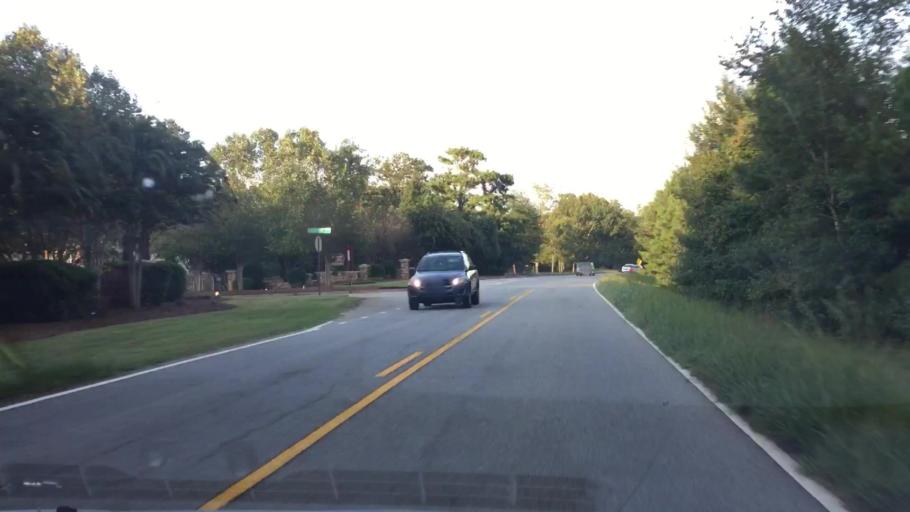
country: US
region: Georgia
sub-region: Henry County
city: Hampton
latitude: 33.4439
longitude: -84.2387
